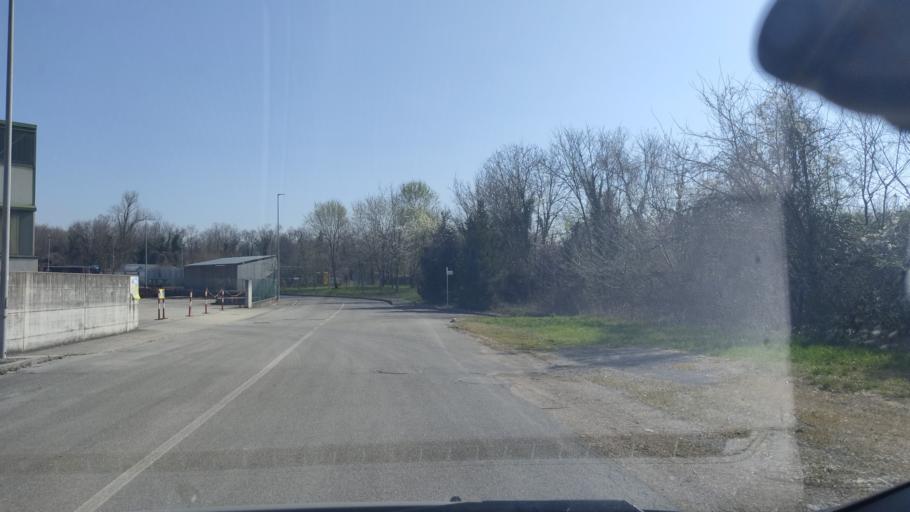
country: IT
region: Friuli Venezia Giulia
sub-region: Provincia di Pordenone
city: Budoia
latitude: 46.0391
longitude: 12.5555
